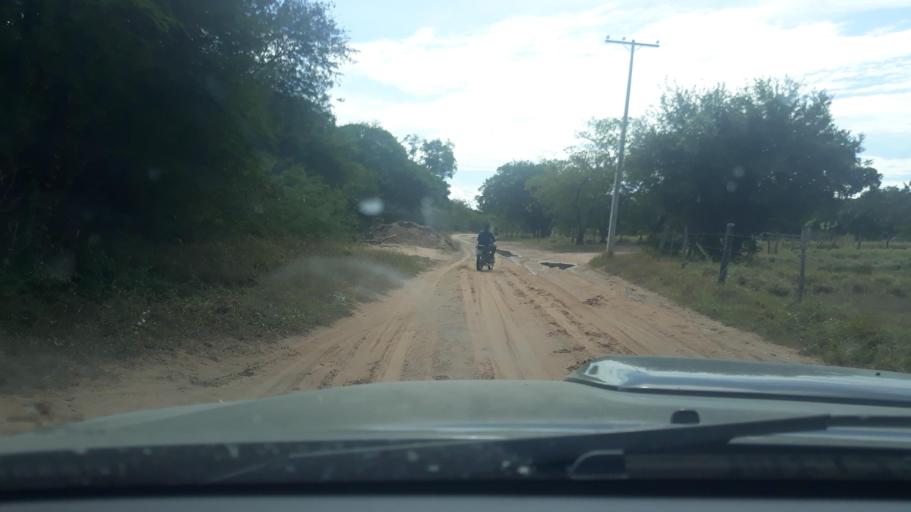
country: BR
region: Bahia
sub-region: Riacho De Santana
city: Riacho de Santana
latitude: -13.8879
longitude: -43.0244
